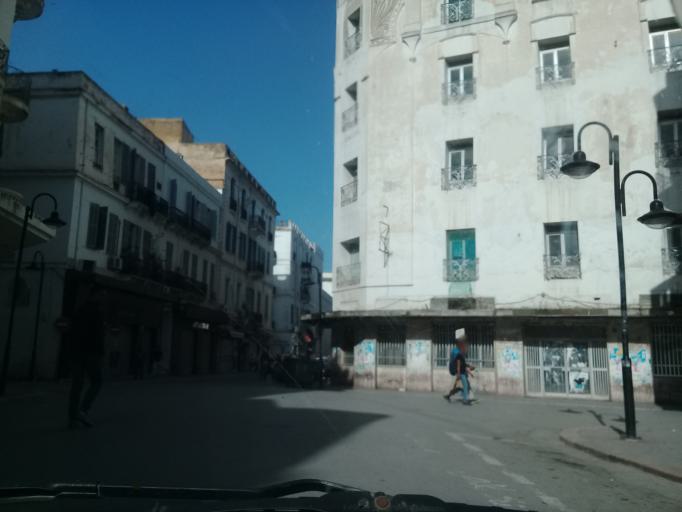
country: TN
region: Tunis
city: Tunis
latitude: 36.8010
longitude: 10.1794
